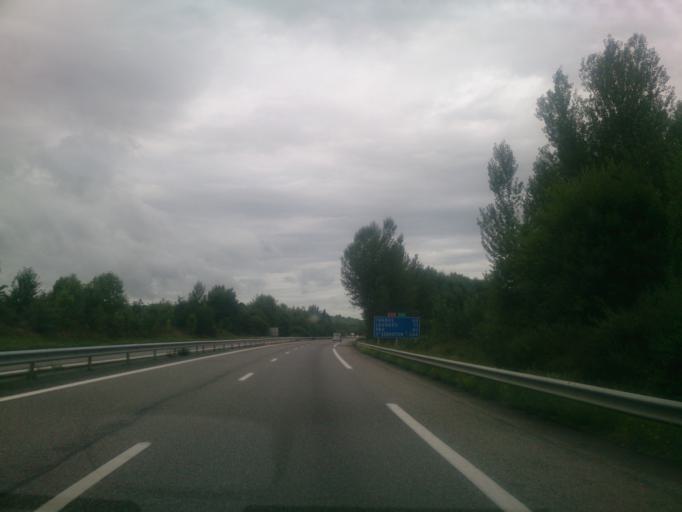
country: FR
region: Midi-Pyrenees
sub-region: Departement de la Haute-Garonne
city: Montrejeau
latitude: 43.0968
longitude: 0.5704
